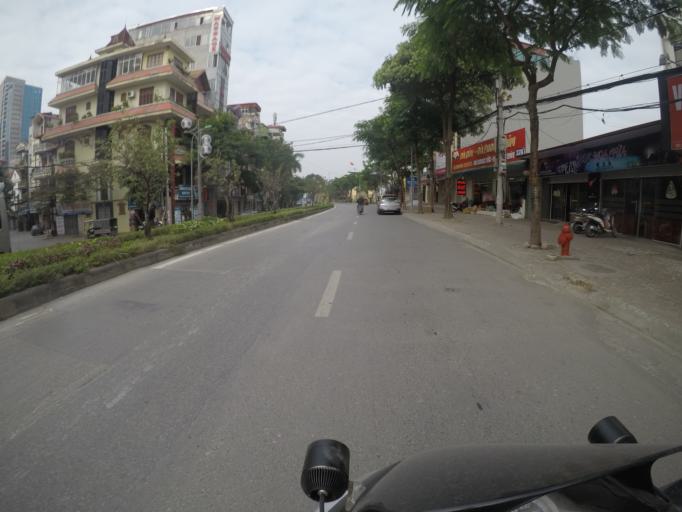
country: VN
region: Ha Noi
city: Tay Ho
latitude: 21.0667
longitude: 105.8108
